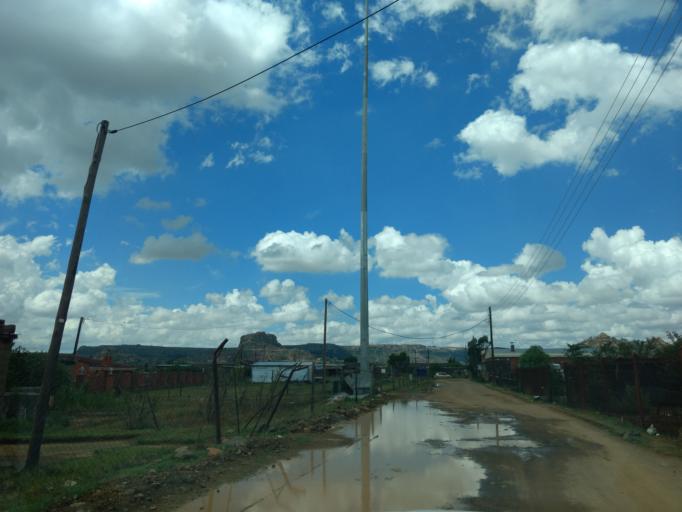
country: LS
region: Maseru
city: Maseru
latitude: -29.3678
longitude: 27.5136
